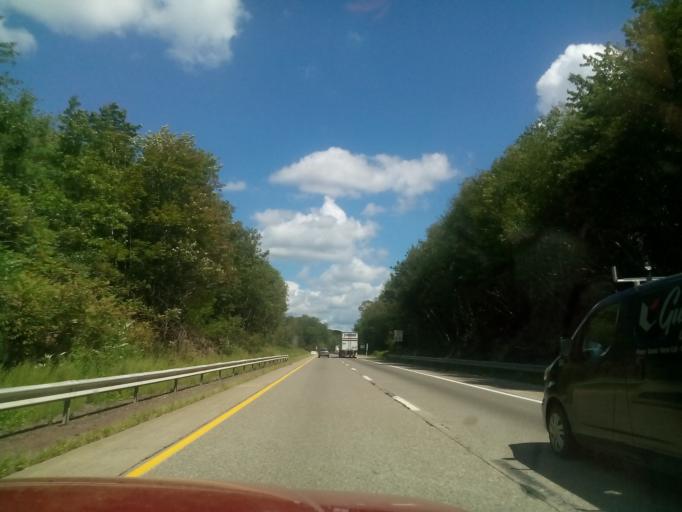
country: US
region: Pennsylvania
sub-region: Luzerne County
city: Conyngham
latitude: 41.0299
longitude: -76.0704
